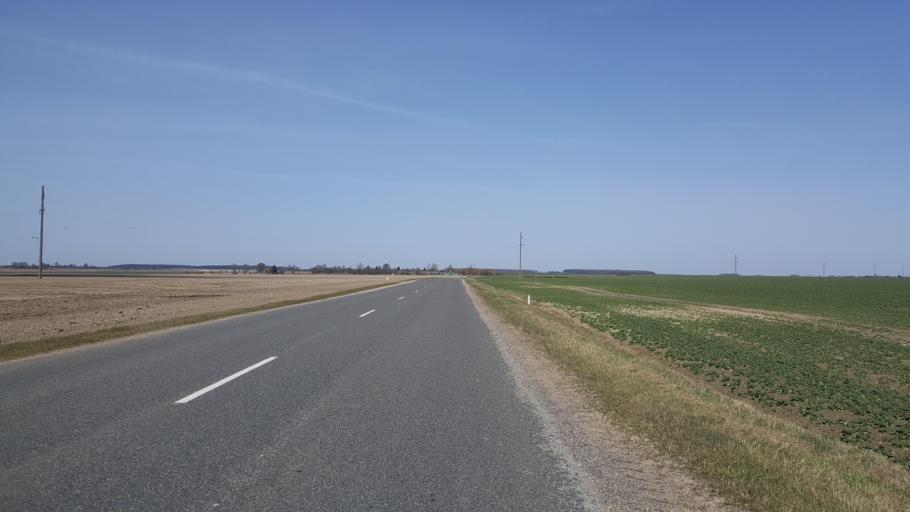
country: BY
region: Brest
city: Kamyanyets
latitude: 52.4183
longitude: 23.7797
